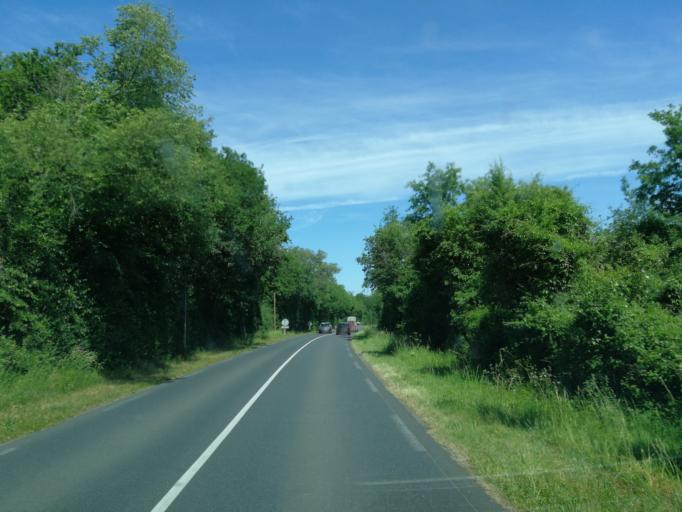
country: FR
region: Poitou-Charentes
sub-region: Departement des Deux-Sevres
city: Saint-Leger-de-Montbrun
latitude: 46.9745
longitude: -0.1063
